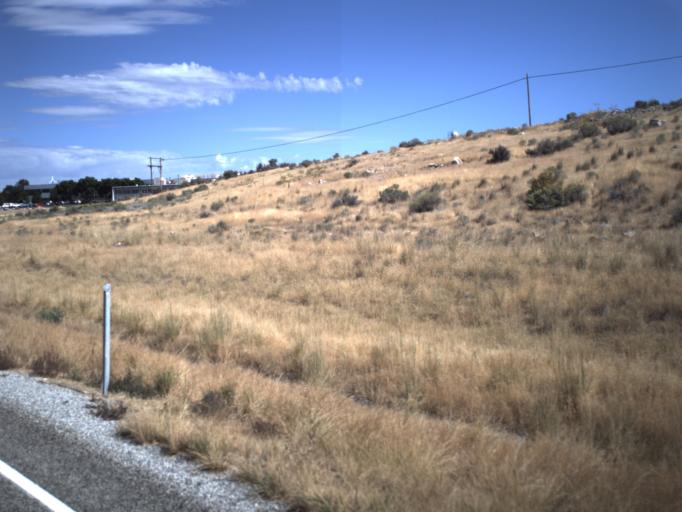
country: US
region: Utah
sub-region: Box Elder County
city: Tremonton
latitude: 41.6554
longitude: -112.4401
